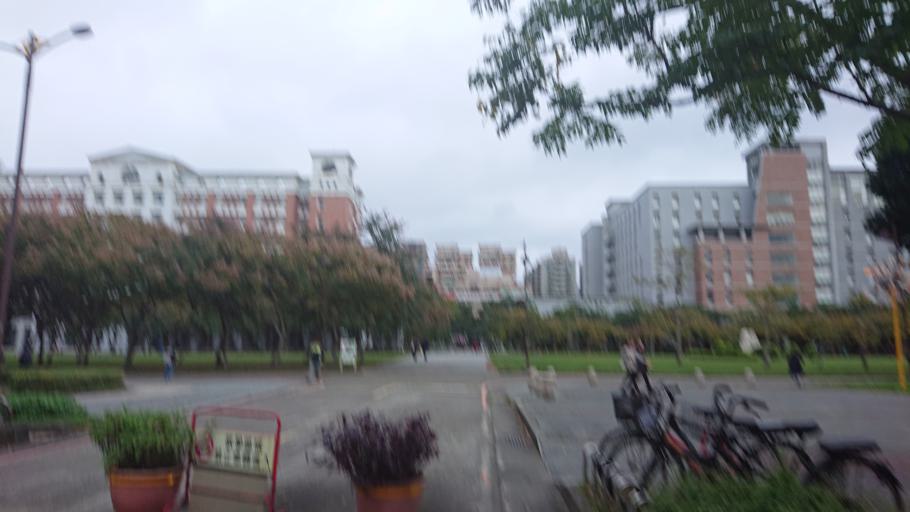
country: TW
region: Taiwan
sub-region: Taoyuan
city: Taoyuan
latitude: 24.9450
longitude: 121.3714
